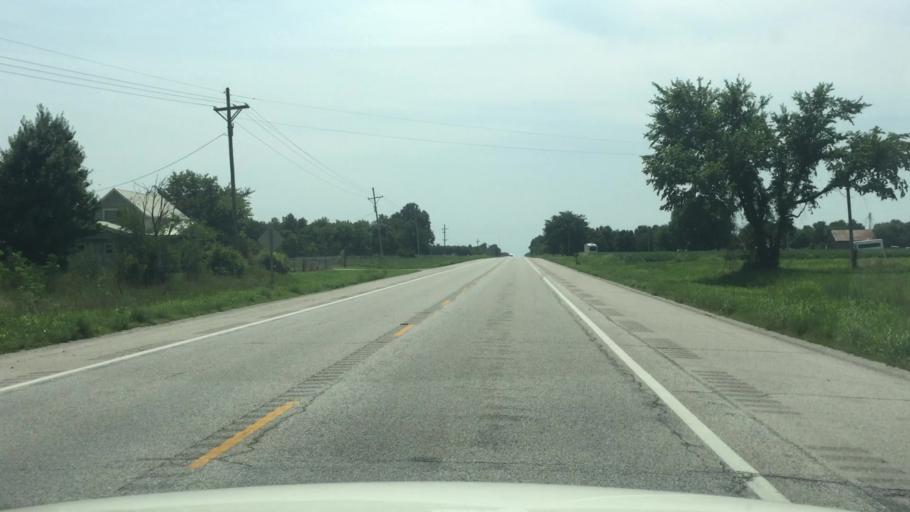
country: US
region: Kansas
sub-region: Cherokee County
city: Galena
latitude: 37.1614
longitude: -94.7044
